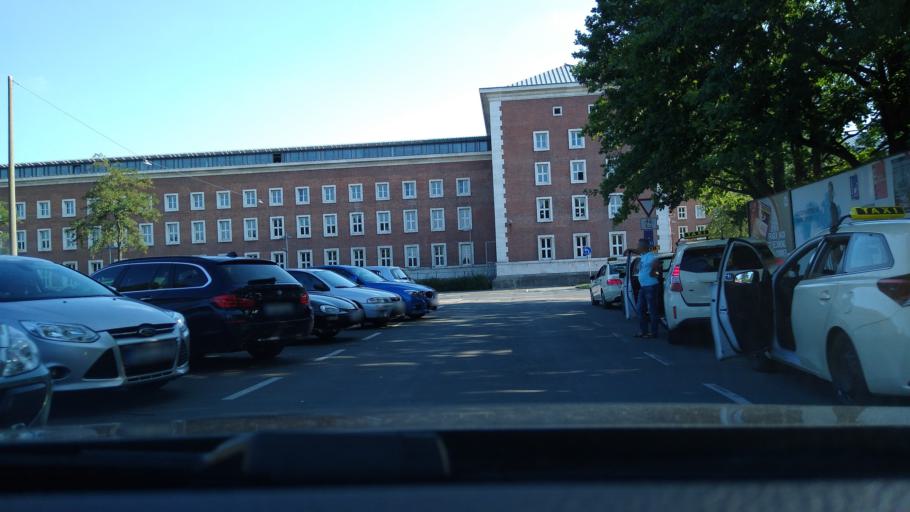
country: DE
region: Bavaria
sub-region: Regierungsbezirk Mittelfranken
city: Nuernberg
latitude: 49.4317
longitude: 11.0985
